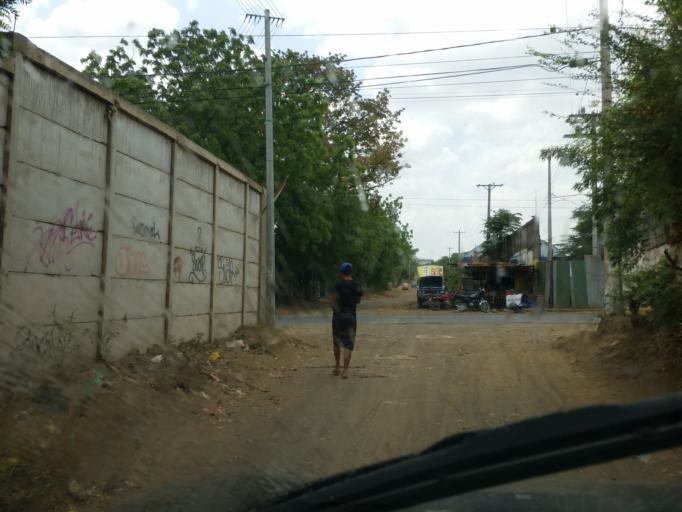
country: NI
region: Managua
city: Managua
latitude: 12.1233
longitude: -86.1935
